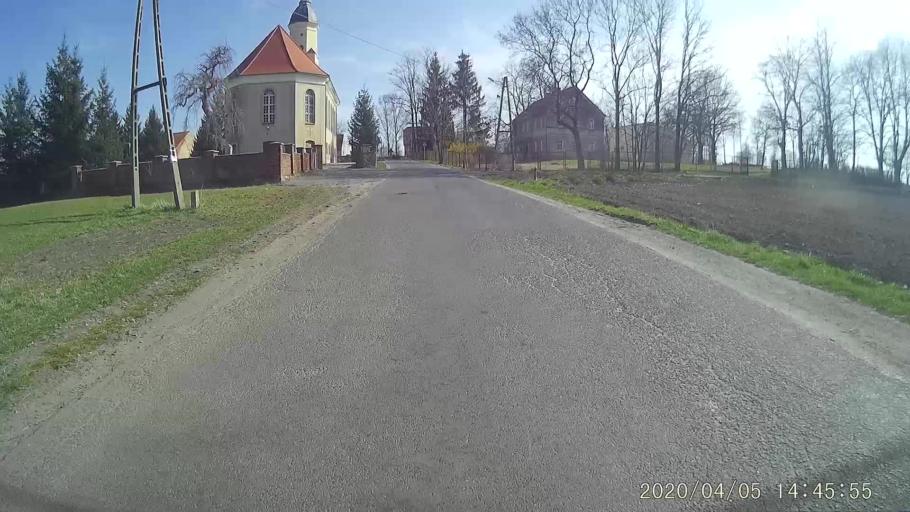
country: PL
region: Lower Silesian Voivodeship
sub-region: Powiat zgorzelecki
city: Sulikow
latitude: 51.0545
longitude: 15.1084
